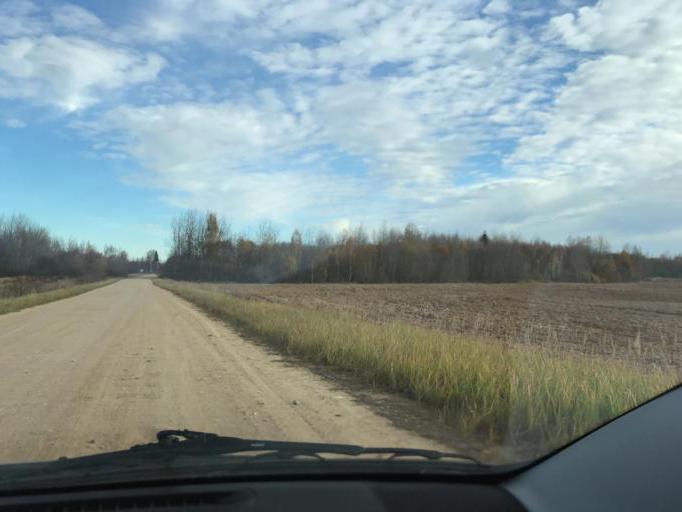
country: BY
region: Vitebsk
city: Haradok
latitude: 55.4546
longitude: 30.0404
